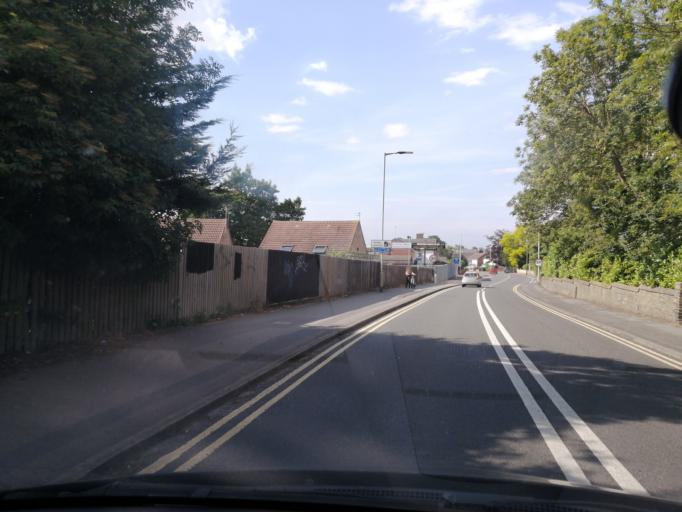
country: GB
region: England
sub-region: Peterborough
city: Peterborough
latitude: 52.5544
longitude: -0.2492
